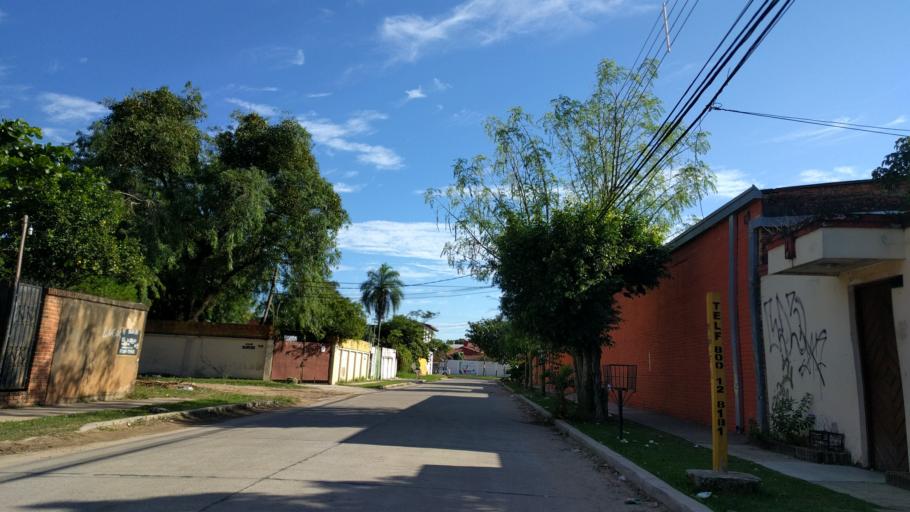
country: BO
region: Santa Cruz
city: Santa Cruz de la Sierra
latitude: -17.7981
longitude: -63.2187
